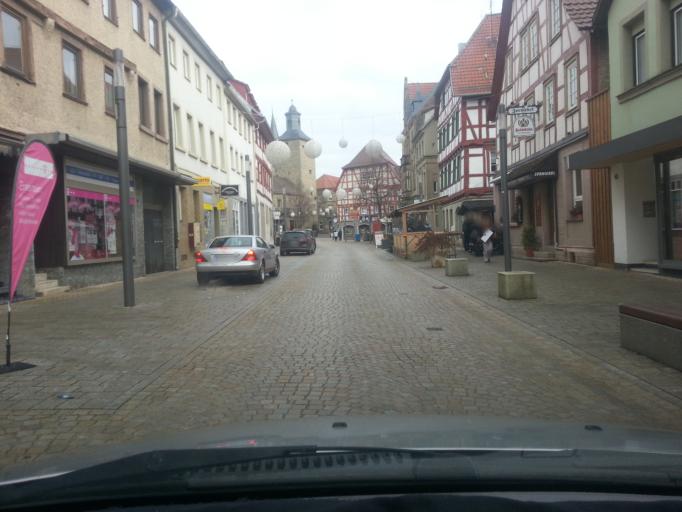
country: DE
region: Baden-Wuerttemberg
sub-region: Regierungsbezirk Stuttgart
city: Eppingen
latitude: 49.1364
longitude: 8.9085
